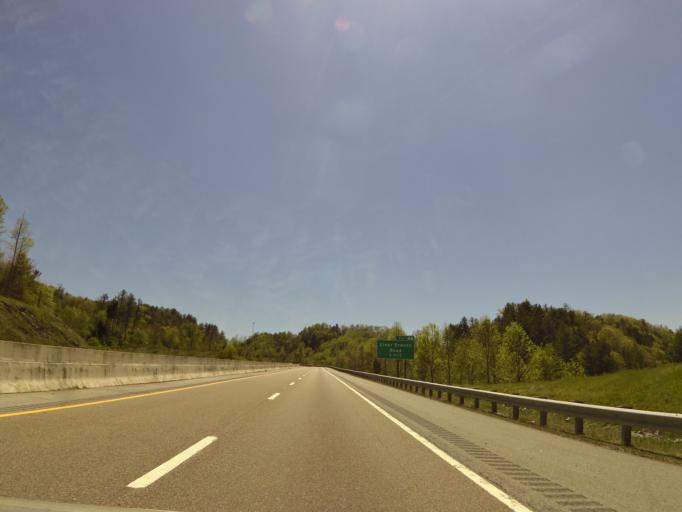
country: US
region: Tennessee
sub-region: Unicoi County
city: Banner Hill
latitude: 36.0669
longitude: -82.5074
